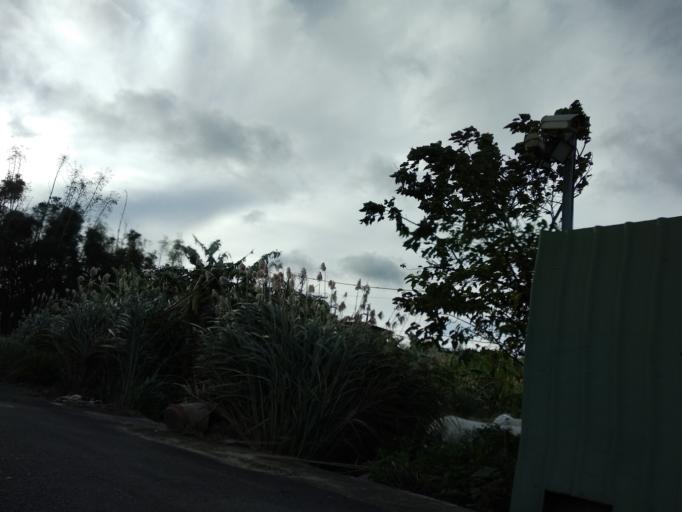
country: TW
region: Taiwan
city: Daxi
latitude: 24.9304
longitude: 121.1931
